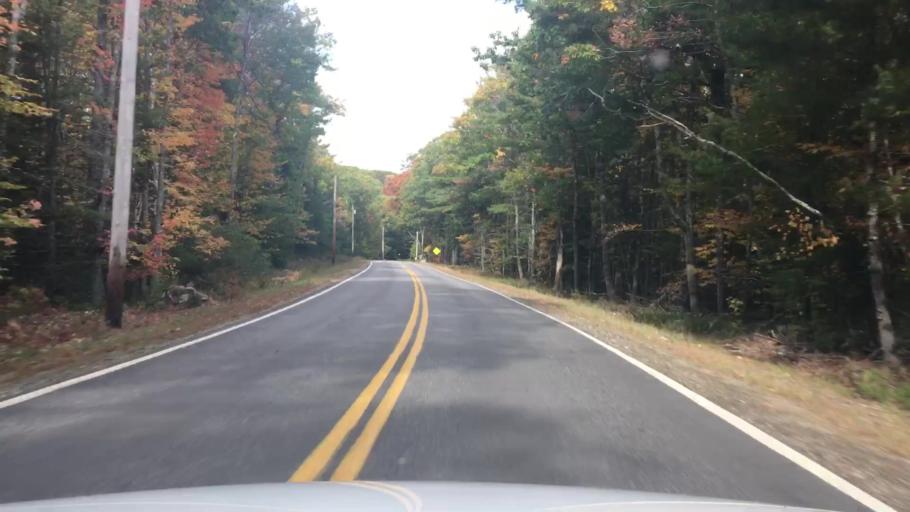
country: US
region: Maine
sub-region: Knox County
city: Hope
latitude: 44.2489
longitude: -69.1264
